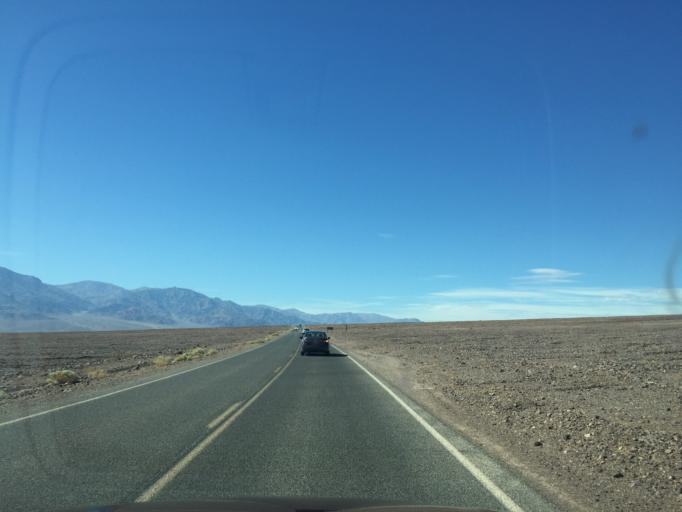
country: US
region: Nevada
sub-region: Nye County
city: Beatty
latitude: 36.2726
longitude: -116.7904
